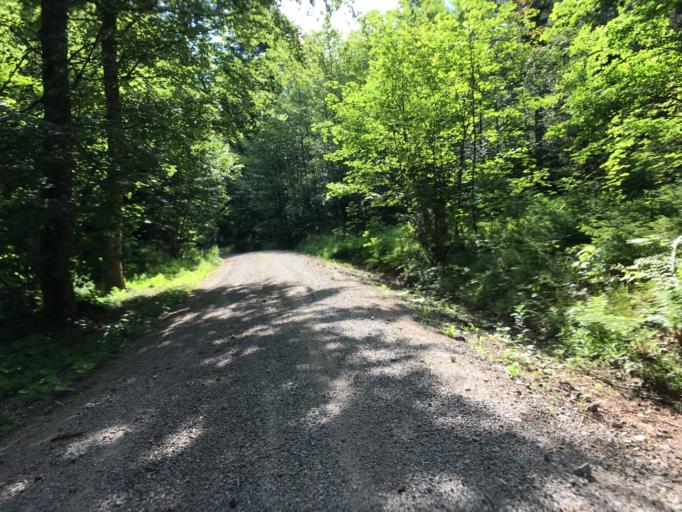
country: DE
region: Baden-Wuerttemberg
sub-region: Karlsruhe Region
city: Freudenstadt
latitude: 48.4331
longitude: 8.4228
